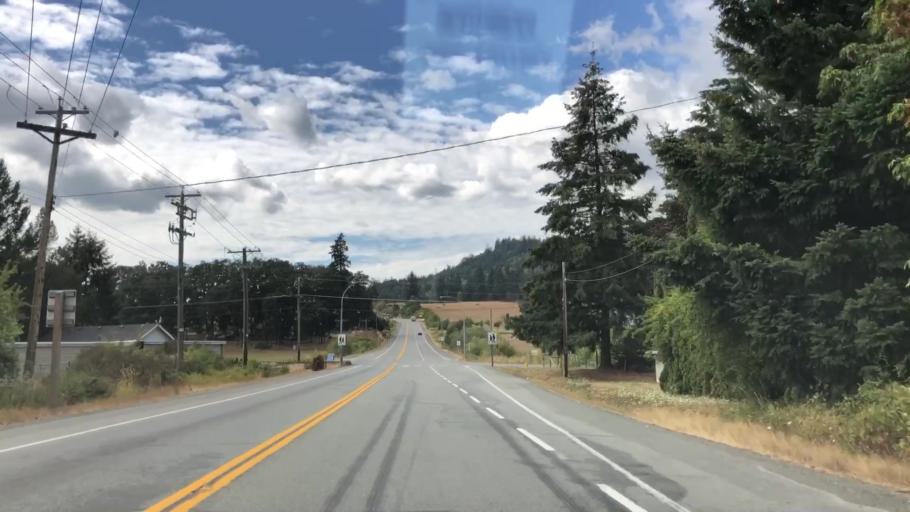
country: CA
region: British Columbia
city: Duncan
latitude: 48.8142
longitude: -123.7347
